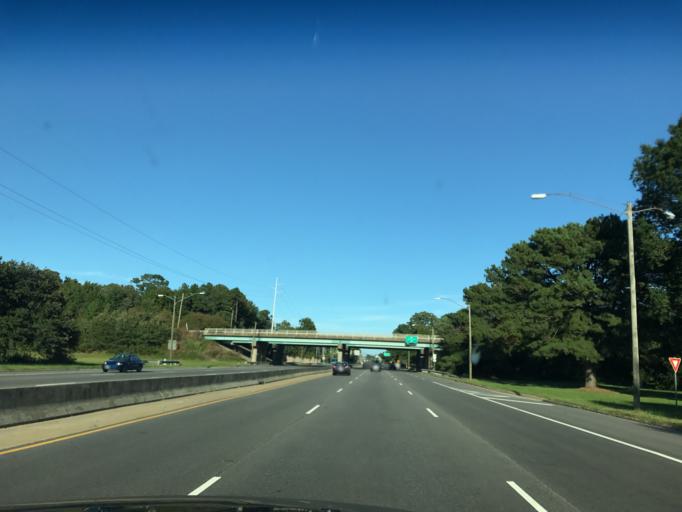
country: US
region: Virginia
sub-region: City of Norfolk
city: Norfolk
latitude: 36.8972
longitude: -76.1464
